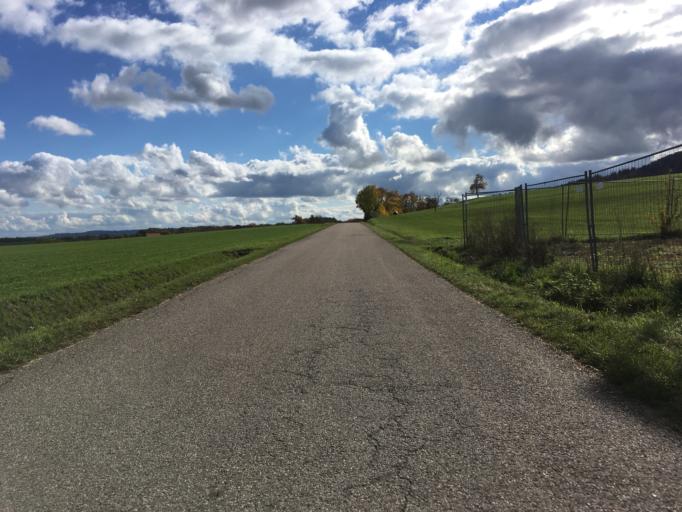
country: DE
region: Baden-Wuerttemberg
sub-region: Regierungsbezirk Stuttgart
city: Waldenburg
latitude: 49.1817
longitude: 9.6772
